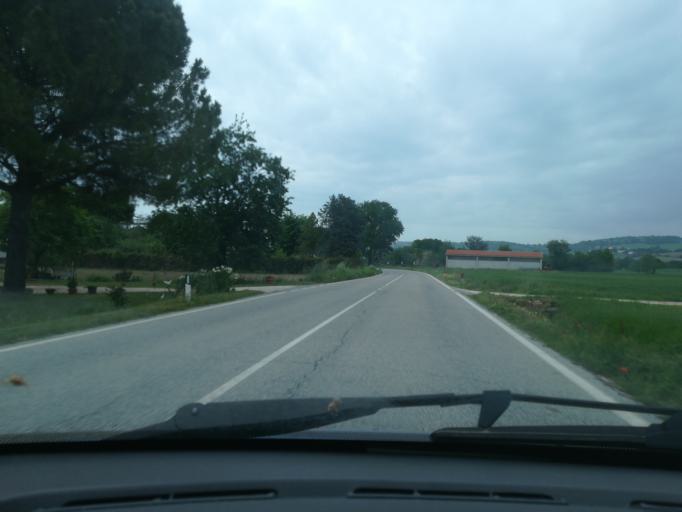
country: IT
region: The Marches
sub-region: Provincia di Macerata
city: Pollenza
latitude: 43.2921
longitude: 13.3662
